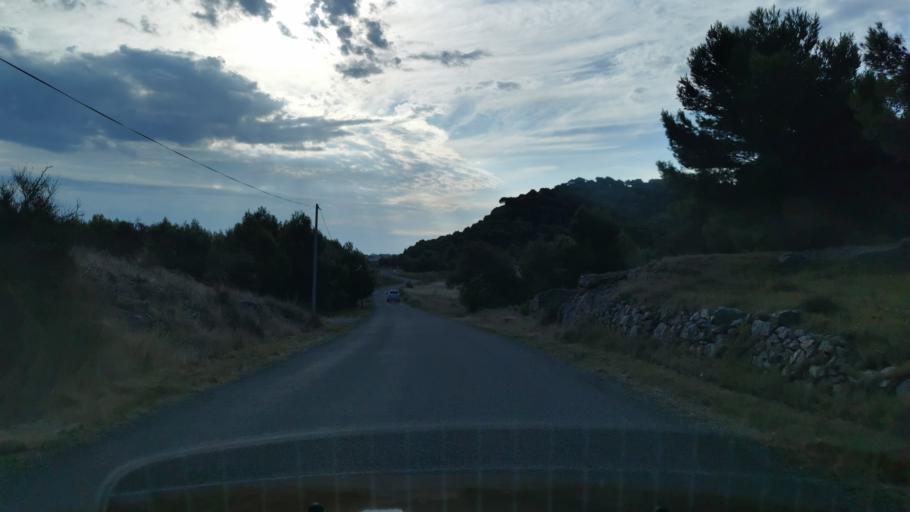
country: FR
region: Languedoc-Roussillon
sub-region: Departement de l'Aude
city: Gruissan
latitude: 43.1077
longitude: 3.0728
